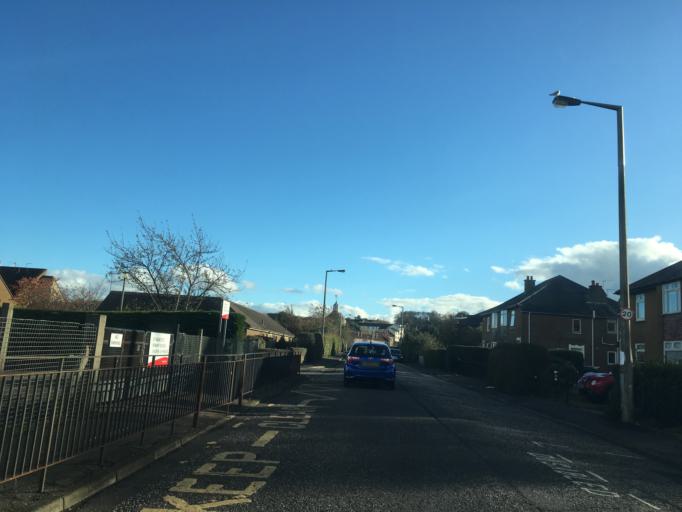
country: GB
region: Scotland
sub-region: Edinburgh
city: Colinton
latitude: 55.9106
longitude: -3.2304
